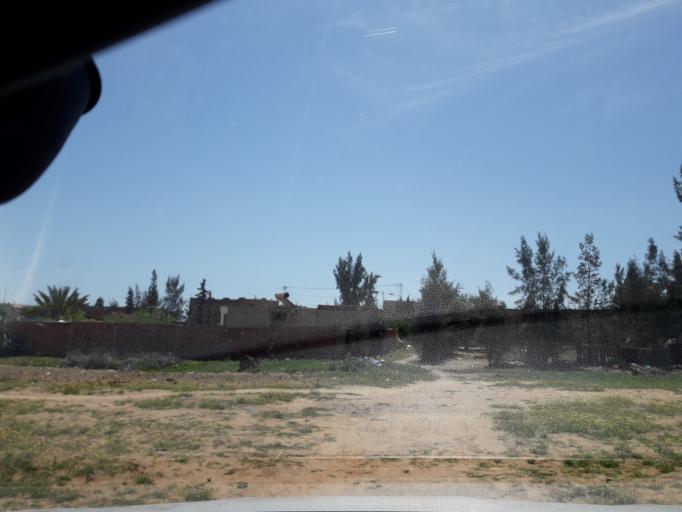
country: TN
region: Safaqis
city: Sfax
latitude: 34.7453
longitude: 10.5136
